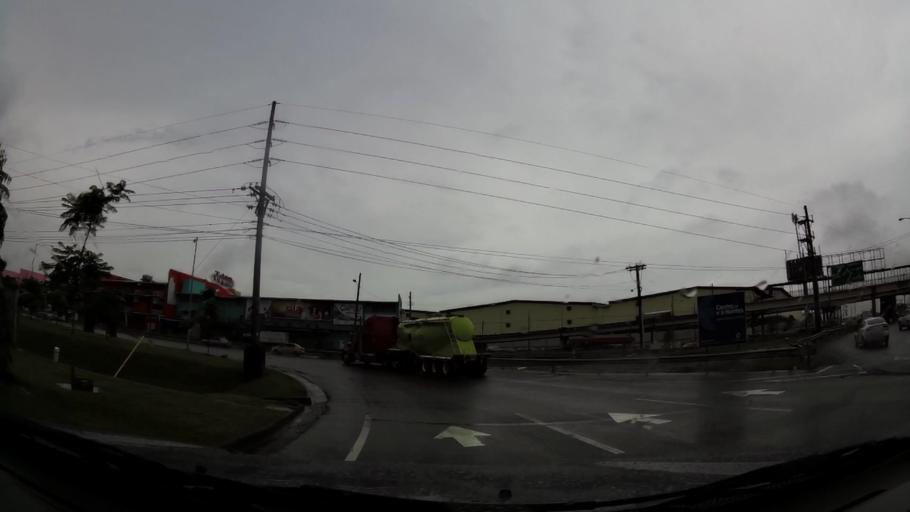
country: PA
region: Colon
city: Arco Iris
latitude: 9.3380
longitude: -79.8812
